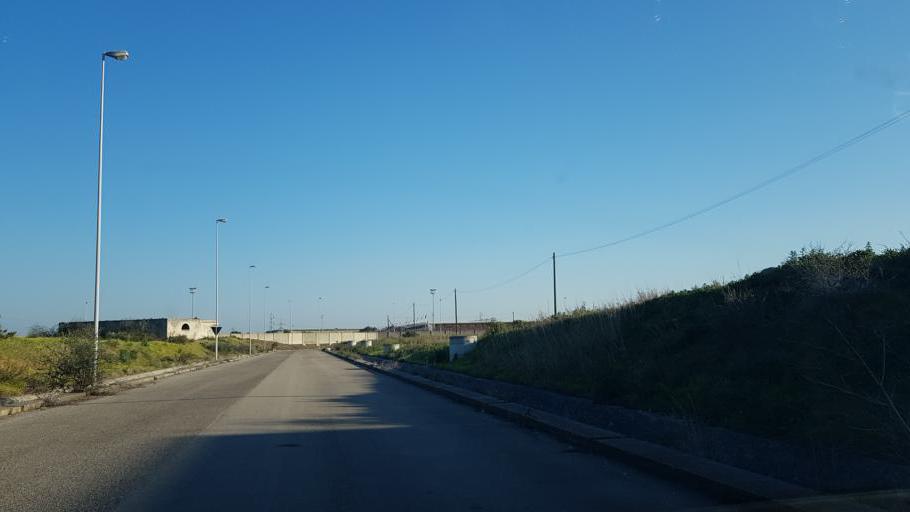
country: IT
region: Apulia
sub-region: Provincia di Brindisi
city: La Rosa
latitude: 40.6263
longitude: 17.9752
